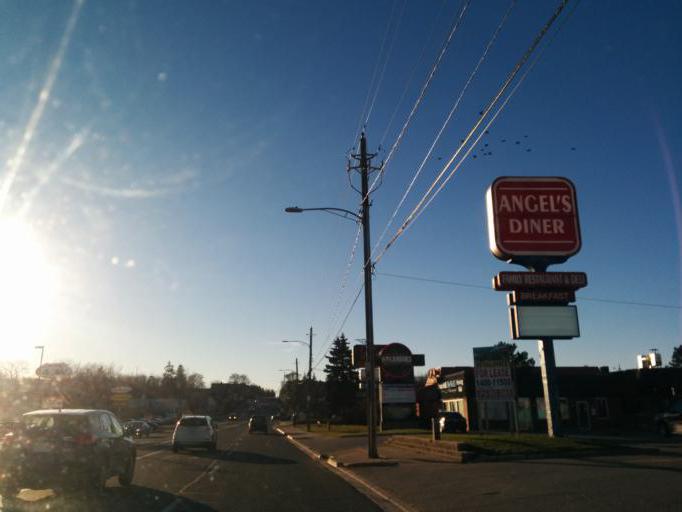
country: CA
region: Ontario
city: Orangeville
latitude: 43.9214
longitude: -80.0879
